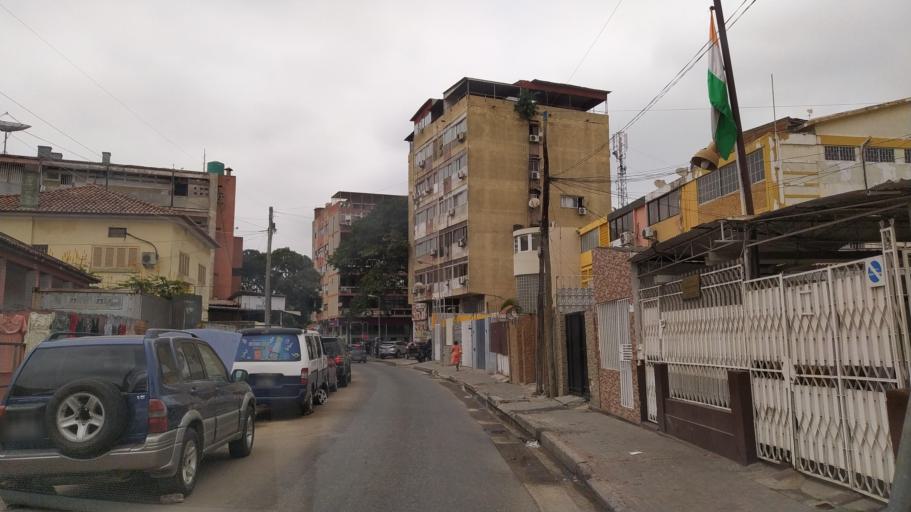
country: AO
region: Luanda
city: Luanda
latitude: -8.8291
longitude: 13.2531
